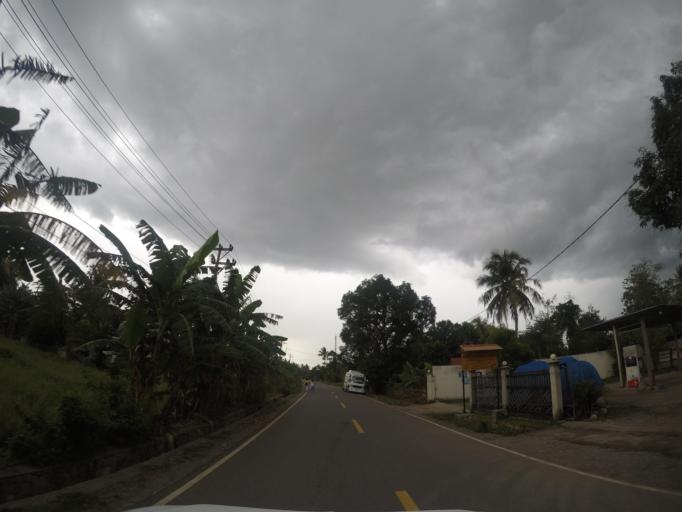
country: TL
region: Bobonaro
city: Maliana
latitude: -8.9643
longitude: 125.2168
